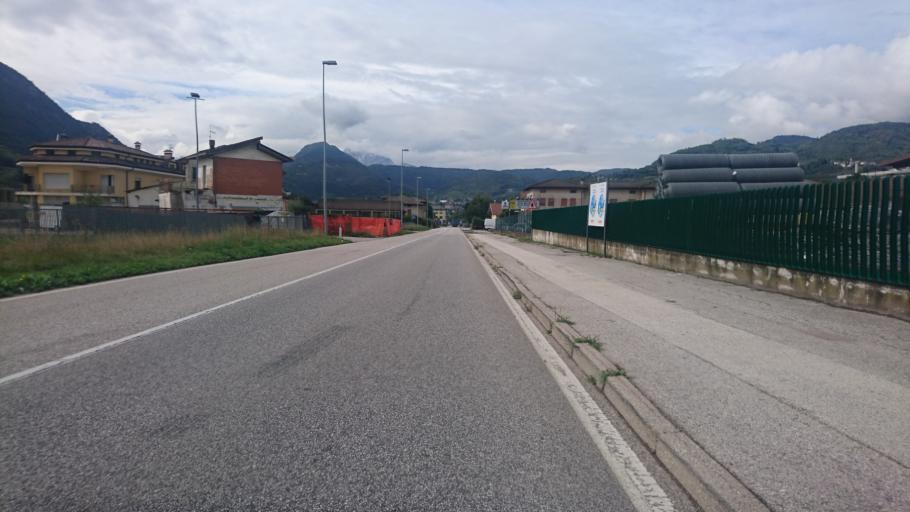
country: IT
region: Trentino-Alto Adige
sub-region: Provincia di Trento
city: Madrano-Canzolino
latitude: 46.0764
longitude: 11.2086
